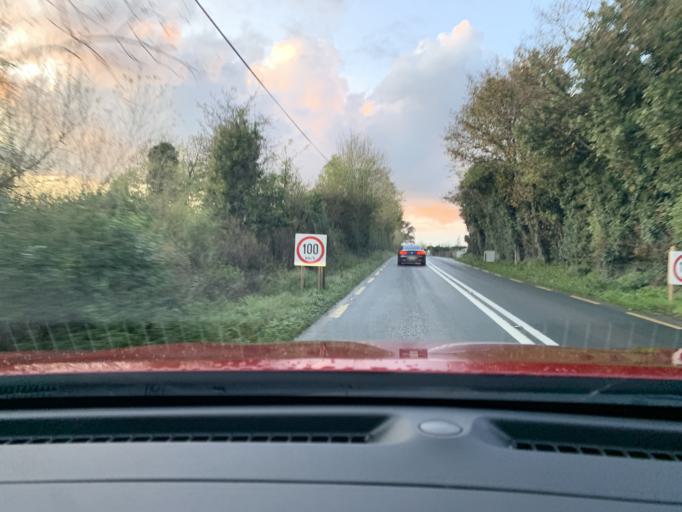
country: IE
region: Connaught
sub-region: Sligo
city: Ballymote
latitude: 54.1032
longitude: -8.4084
